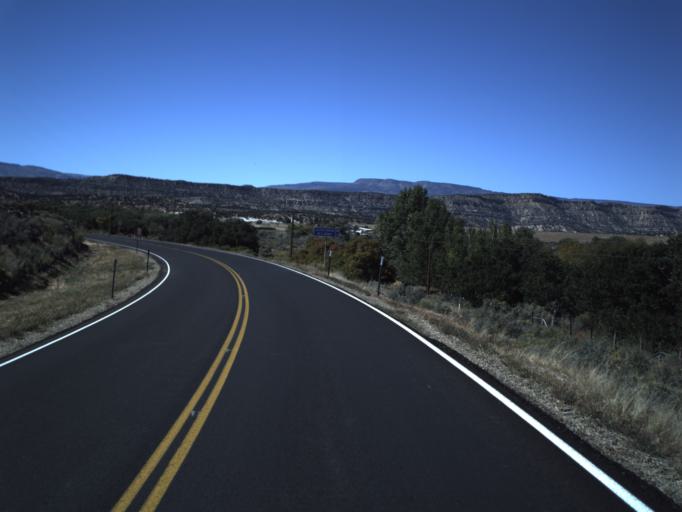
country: US
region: Utah
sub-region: Wayne County
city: Loa
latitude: 37.7774
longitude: -111.6213
